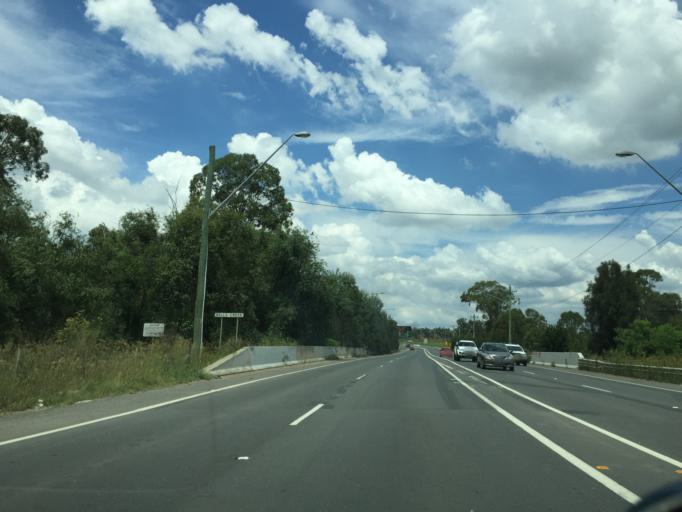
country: AU
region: New South Wales
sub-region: Blacktown
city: Hassall Grove
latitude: -33.7290
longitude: 150.8458
